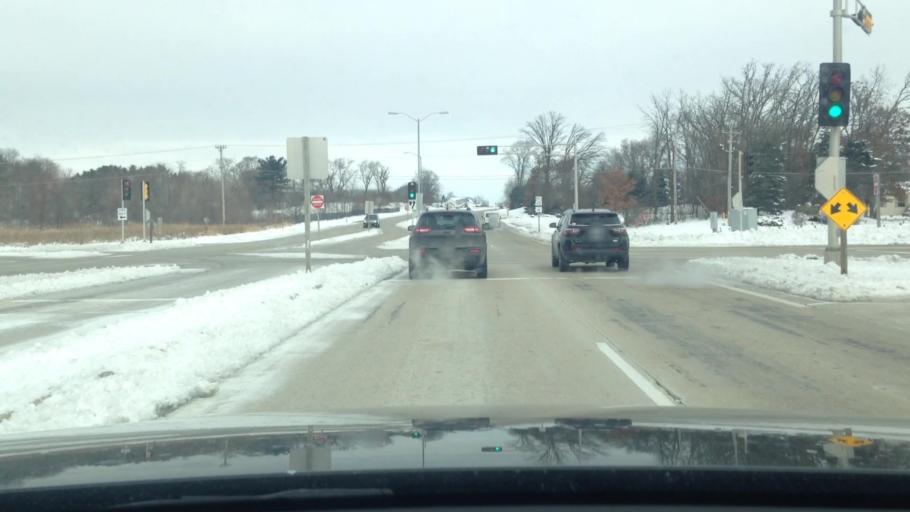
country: US
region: Wisconsin
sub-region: Walworth County
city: Lake Geneva
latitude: 42.5643
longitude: -88.4138
